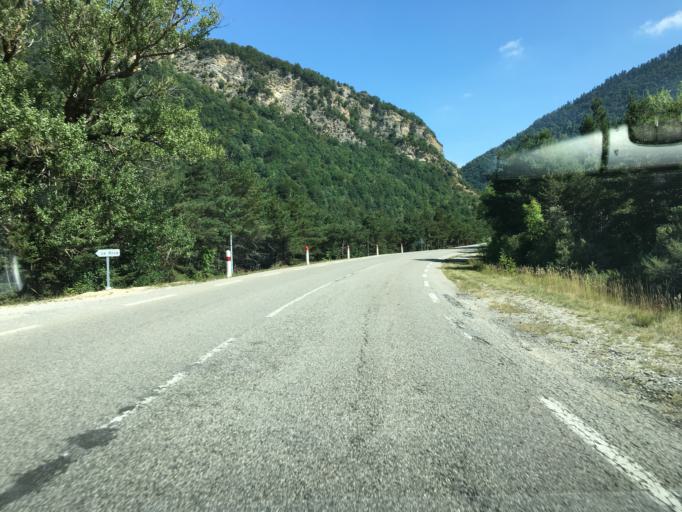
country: FR
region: Provence-Alpes-Cote d'Azur
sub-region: Departement des Hautes-Alpes
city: Veynes
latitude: 44.6393
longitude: 5.6960
